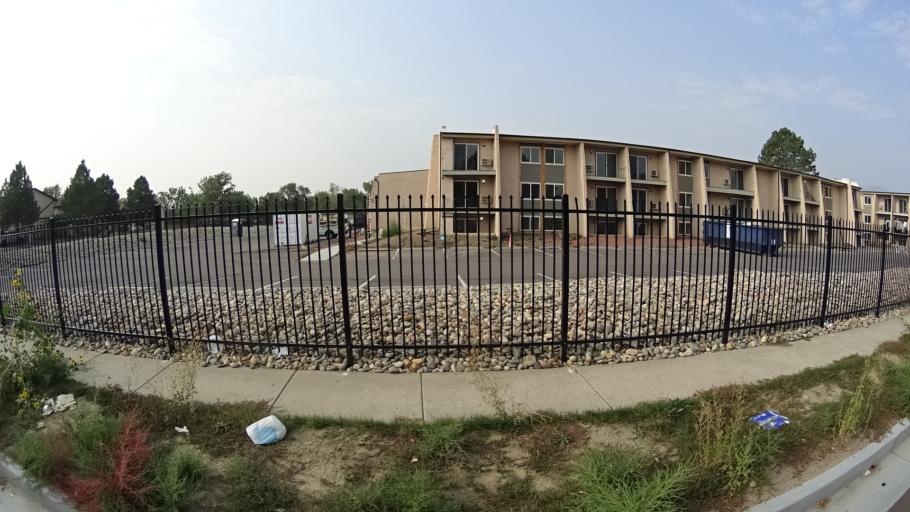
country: US
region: Colorado
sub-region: El Paso County
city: Stratmoor
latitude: 38.8070
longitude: -104.7755
